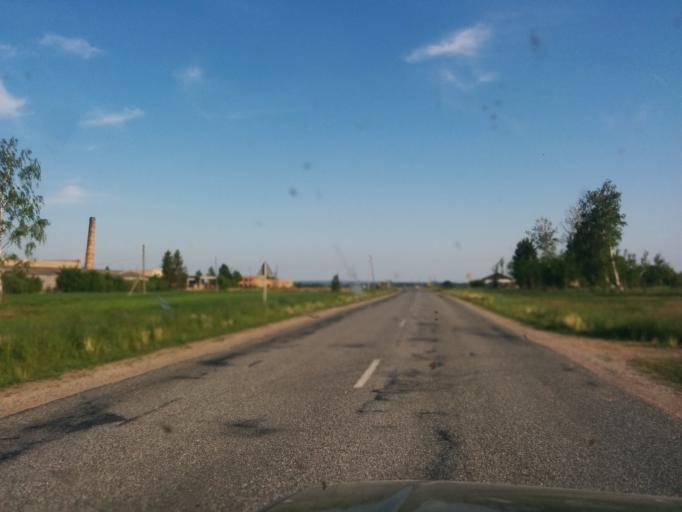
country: LV
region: Talsu Rajons
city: Valdemarpils
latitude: 57.3479
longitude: 22.4992
